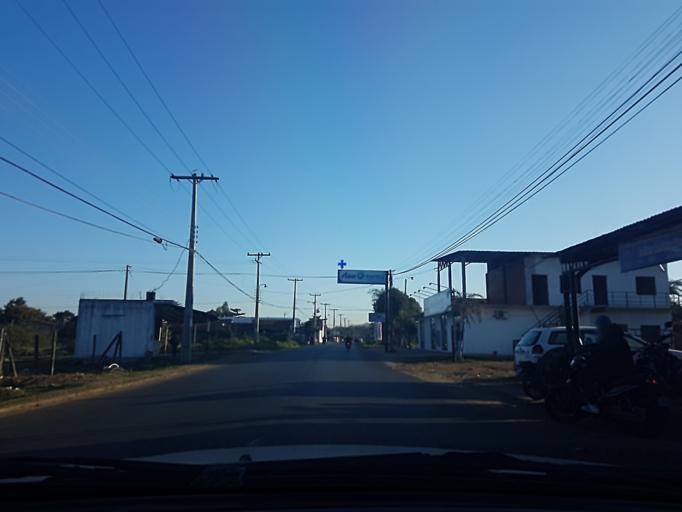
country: PY
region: Central
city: Colonia Mariano Roque Alonso
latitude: -25.2188
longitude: -57.5205
